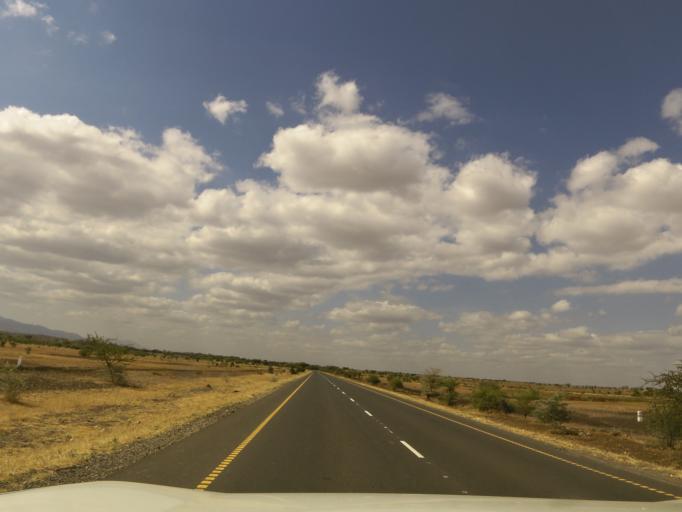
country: TZ
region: Arusha
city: Mto wa Mbu
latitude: -3.5836
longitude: 36.0671
